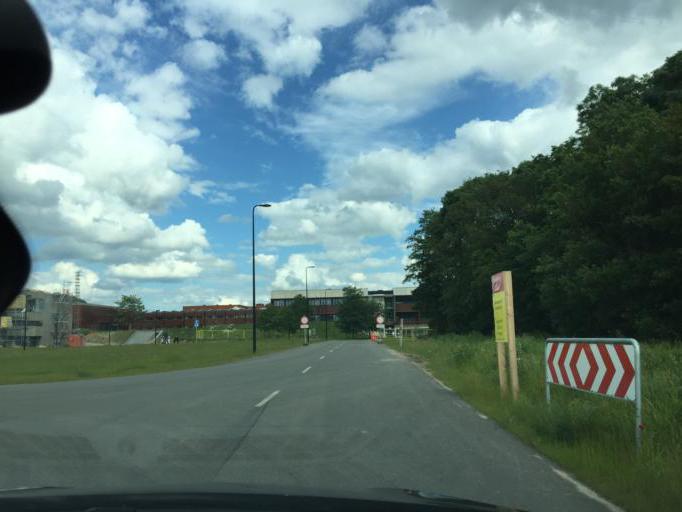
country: DK
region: South Denmark
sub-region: Odense Kommune
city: Neder Holluf
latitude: 55.3670
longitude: 10.4233
